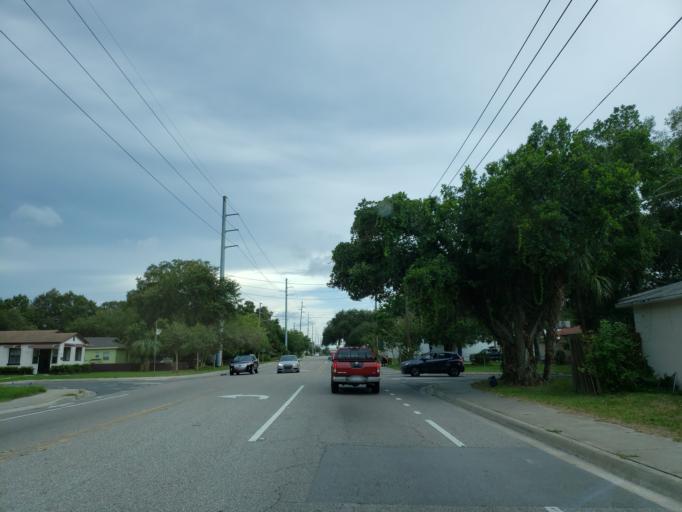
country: US
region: Florida
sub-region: Pinellas County
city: Saint Petersburg
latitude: 27.7653
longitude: -82.6754
